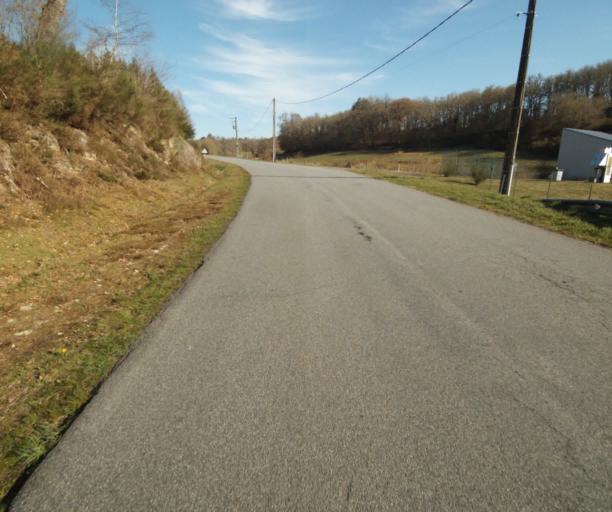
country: FR
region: Limousin
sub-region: Departement de la Correze
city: Correze
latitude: 45.3128
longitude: 1.8868
